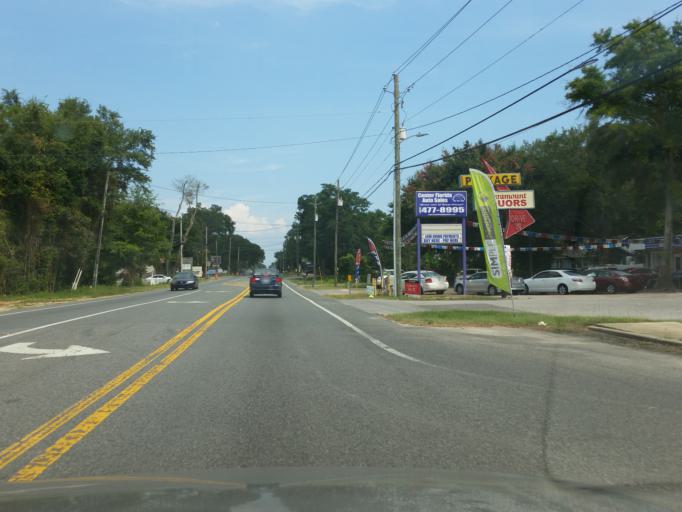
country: US
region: Florida
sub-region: Escambia County
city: Ferry Pass
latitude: 30.5102
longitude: -87.2174
